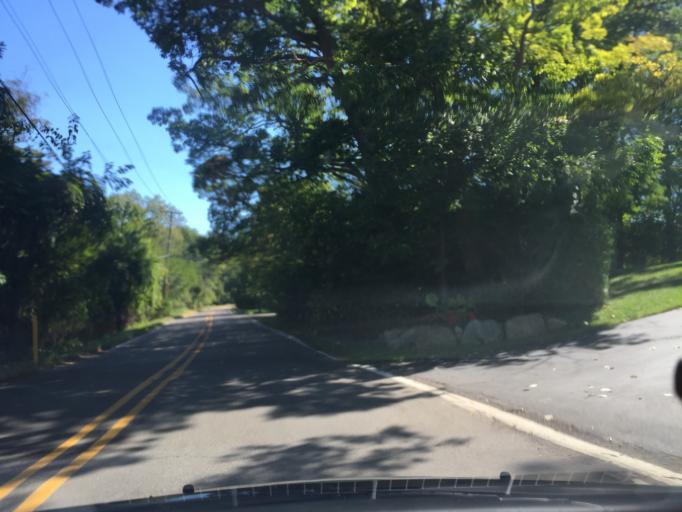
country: US
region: Michigan
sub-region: Oakland County
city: Sylvan Lake
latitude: 42.5930
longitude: -83.2976
